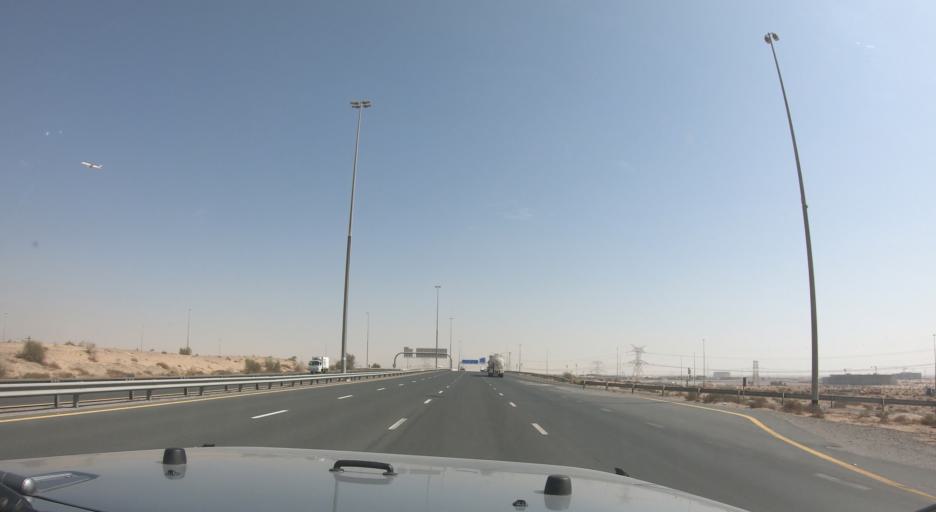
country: AE
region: Ash Shariqah
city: Sharjah
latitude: 25.1645
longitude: 55.4918
